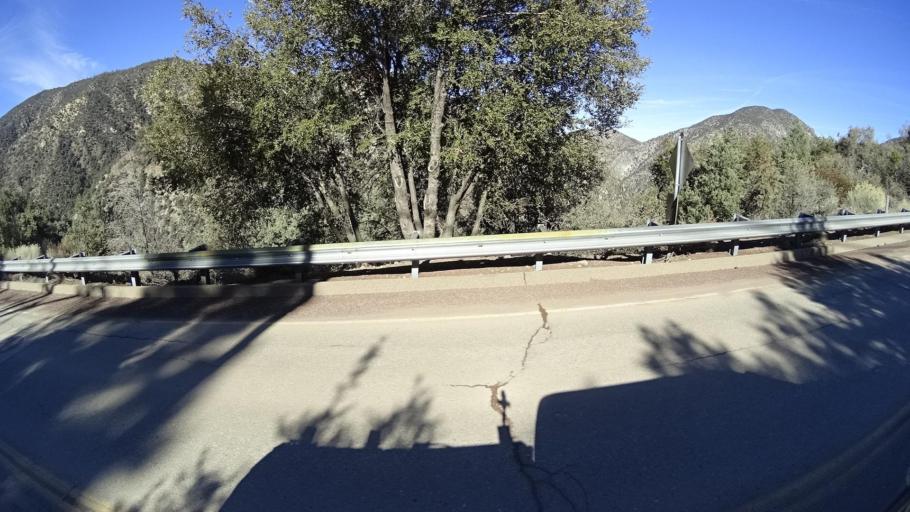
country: US
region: California
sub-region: Kern County
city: Pine Mountain Club
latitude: 34.8519
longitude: -119.1381
